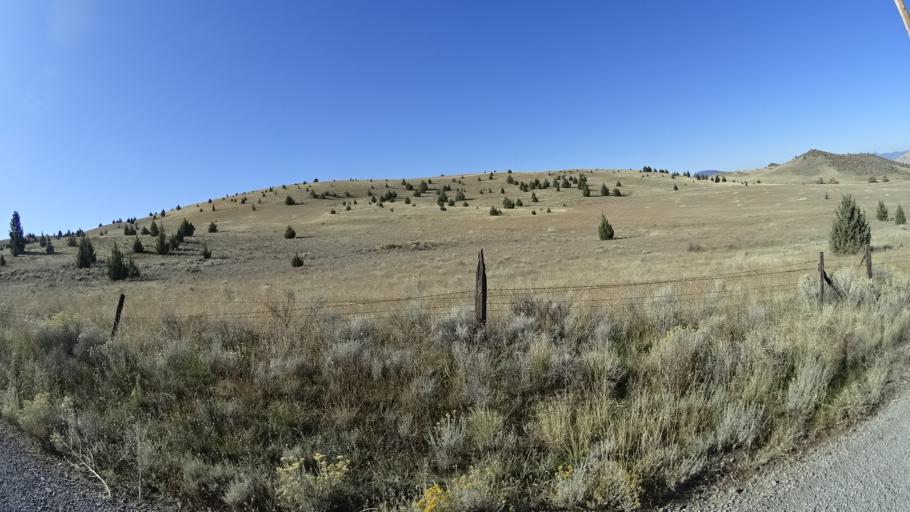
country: US
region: California
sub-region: Siskiyou County
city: Montague
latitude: 41.7789
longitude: -122.3587
